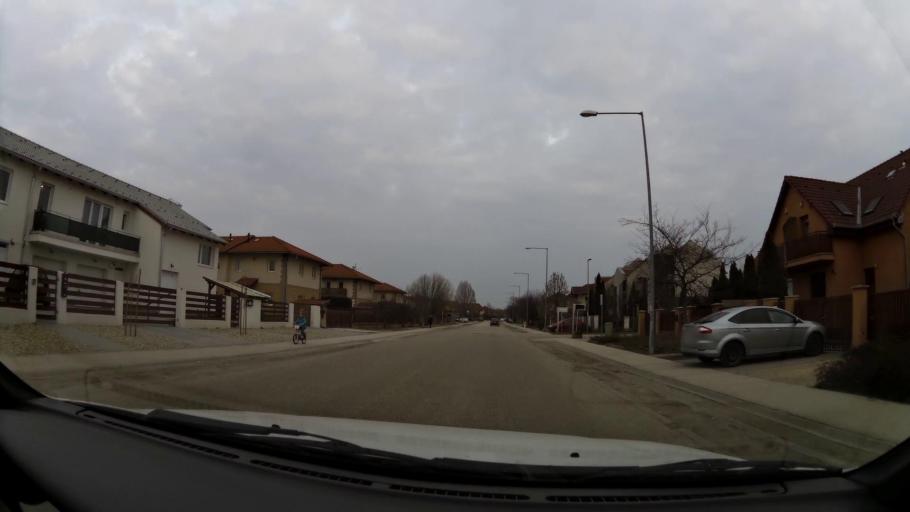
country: HU
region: Budapest
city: Budapest XVII. keruelet
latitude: 47.4713
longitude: 19.2205
